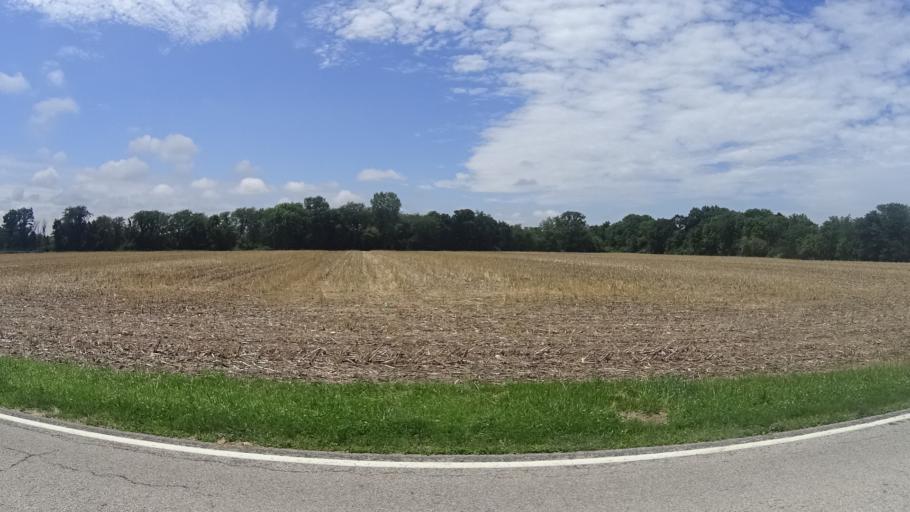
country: US
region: Ohio
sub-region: Erie County
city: Milan
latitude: 41.3205
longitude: -82.5808
